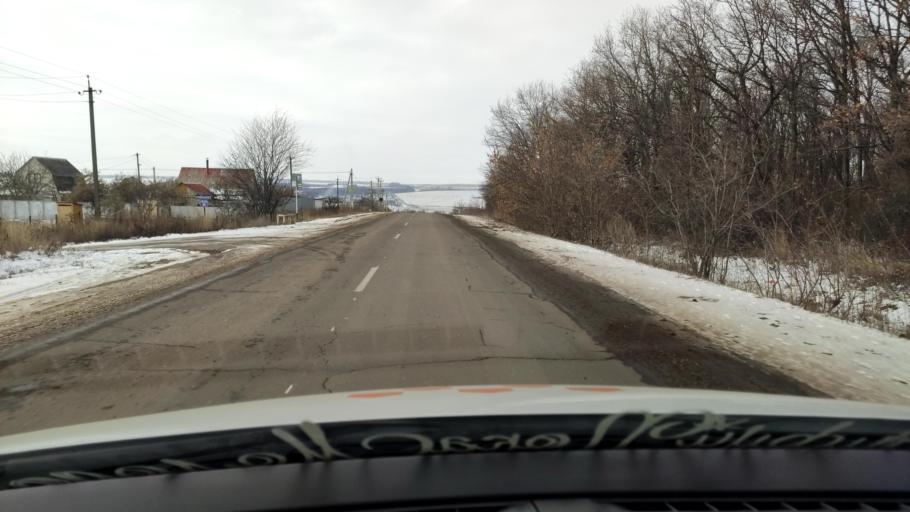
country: RU
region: Voronezj
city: Semiluki
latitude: 51.7489
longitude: 39.0404
